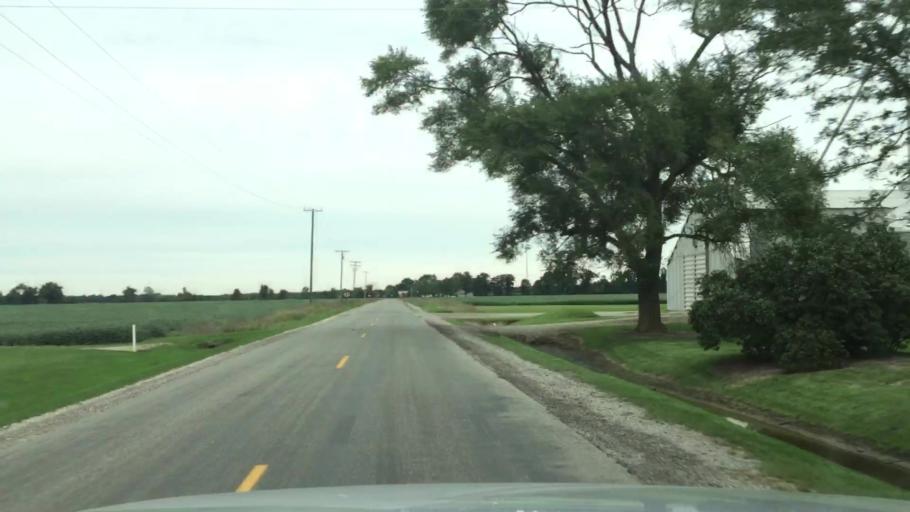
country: US
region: Michigan
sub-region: Washtenaw County
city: Milan
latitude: 42.0759
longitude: -83.7356
